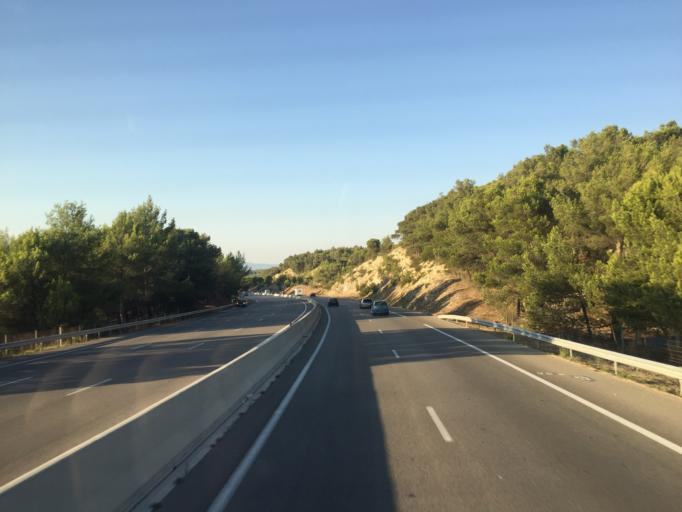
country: FR
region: Provence-Alpes-Cote d'Azur
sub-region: Departement des Bouches-du-Rhone
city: Venelles
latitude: 43.6018
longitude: 5.4961
